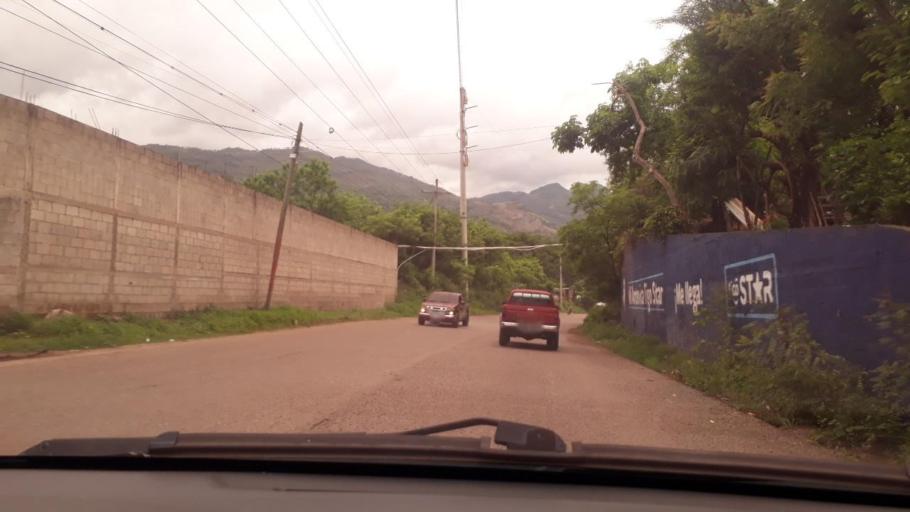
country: GT
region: Chiquimula
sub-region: Municipio de Jocotan
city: Jocotan
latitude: 14.8003
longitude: -89.3938
